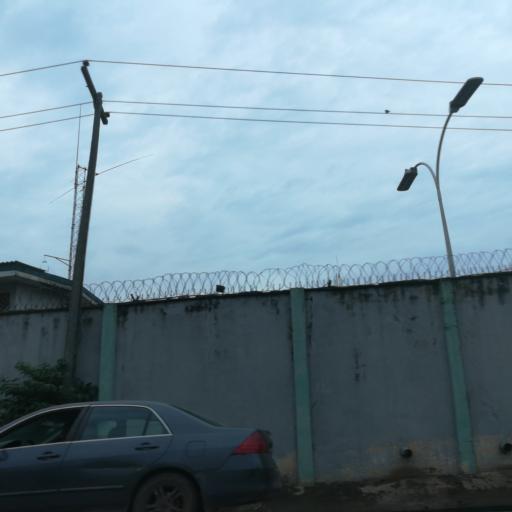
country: NG
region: Lagos
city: Ikeja
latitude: 6.5936
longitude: 3.3471
